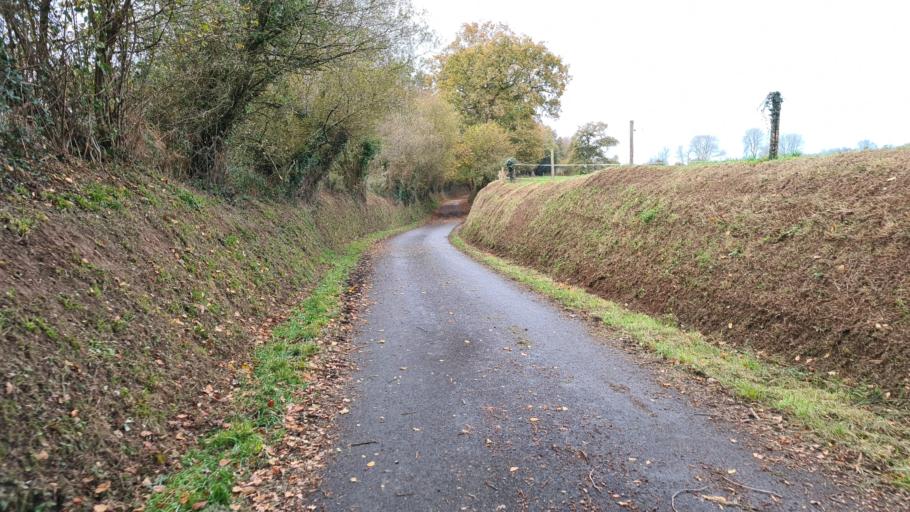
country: FR
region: Lower Normandy
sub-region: Departement de la Manche
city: La Haye-Pesnel
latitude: 48.7874
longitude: -1.4075
